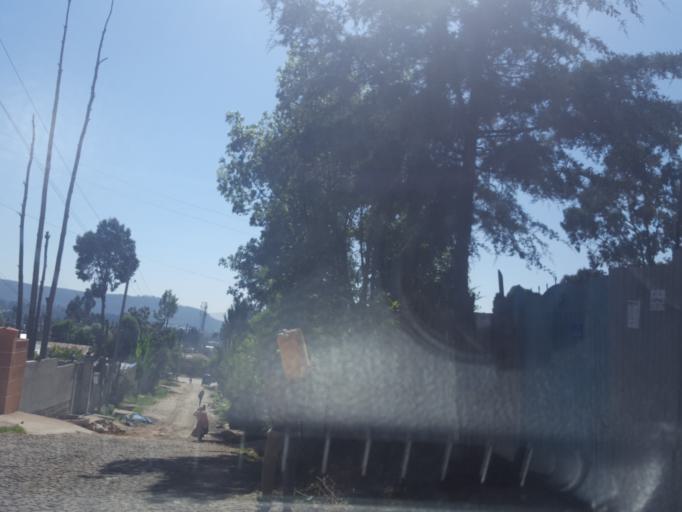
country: ET
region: Adis Abeba
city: Addis Ababa
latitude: 9.0635
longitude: 38.7422
